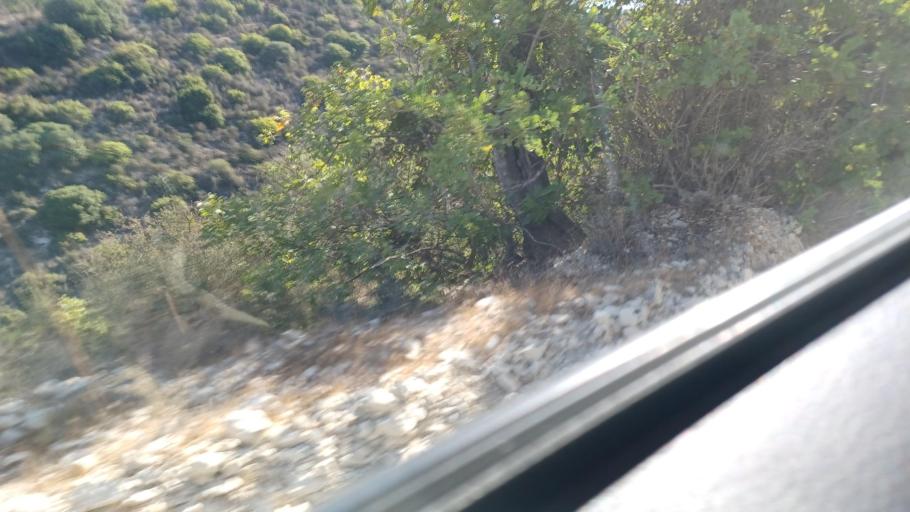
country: CY
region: Pafos
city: Tala
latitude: 34.8647
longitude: 32.4422
